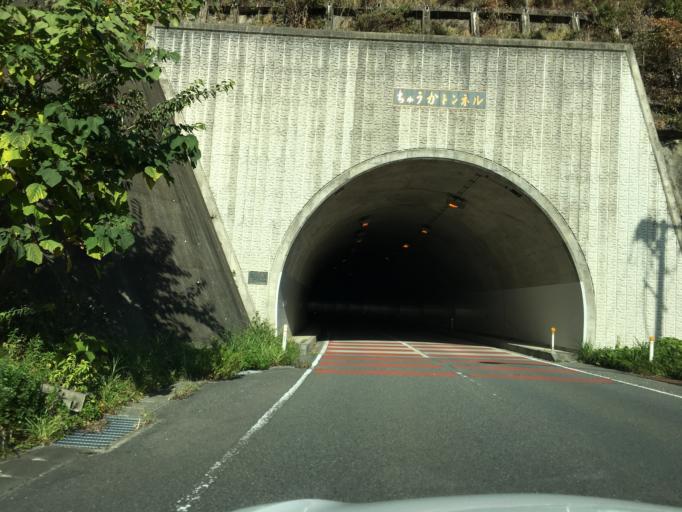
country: JP
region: Fukushima
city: Namie
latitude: 37.3615
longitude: 140.9523
